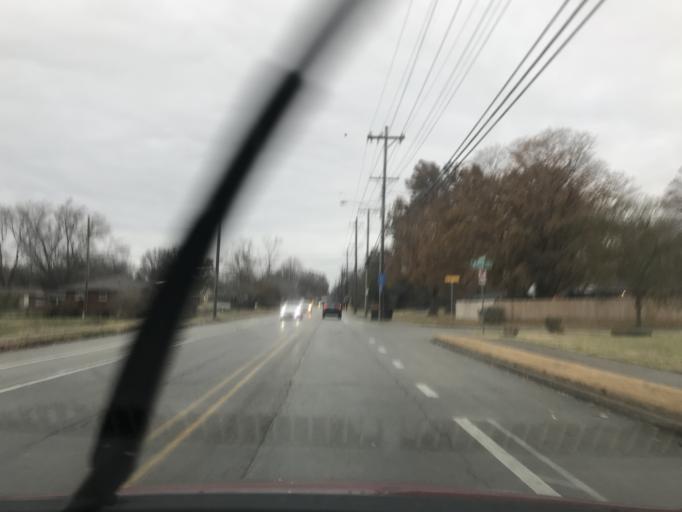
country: US
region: Kentucky
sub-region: Jefferson County
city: West Buechel
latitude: 38.2104
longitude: -85.6653
